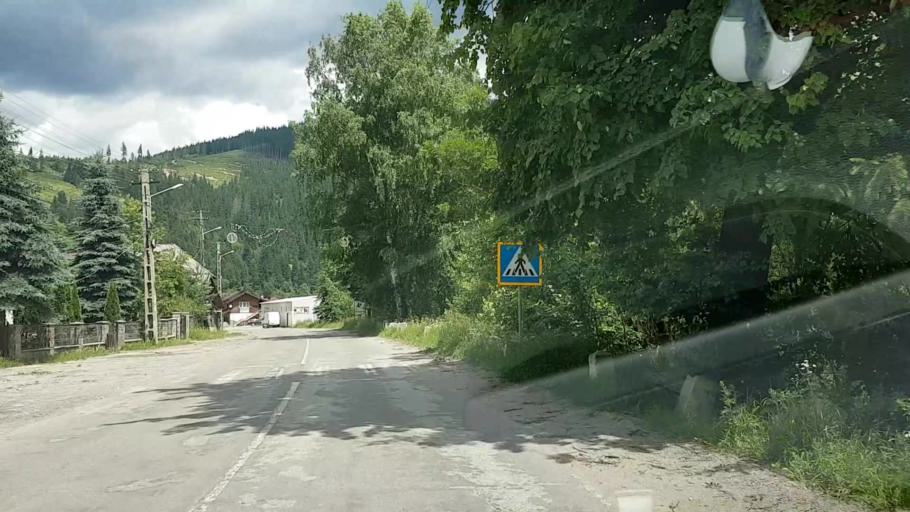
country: RO
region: Suceava
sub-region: Comuna Brosteni
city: Brosteni
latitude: 47.2382
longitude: 25.6979
